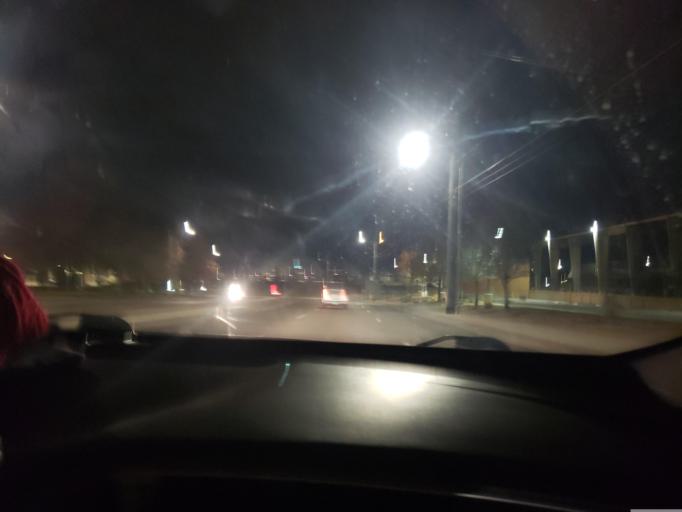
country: US
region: New Mexico
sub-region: Bernalillo County
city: Albuquerque
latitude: 35.0697
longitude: -106.6245
